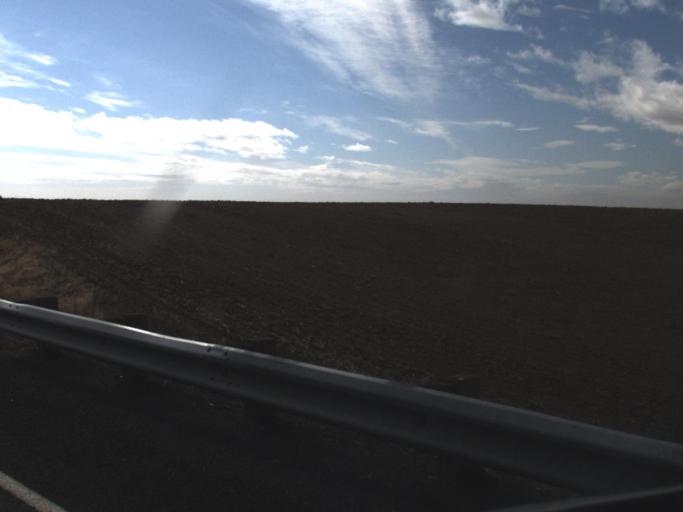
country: US
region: Washington
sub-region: Okanogan County
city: Coulee Dam
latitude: 47.7938
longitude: -118.7218
